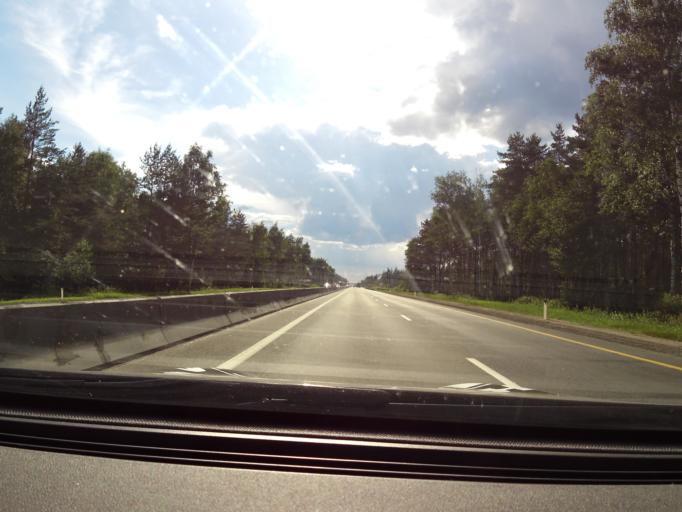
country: RU
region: Nizjnij Novgorod
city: Pyra
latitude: 56.2943
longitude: 43.3763
